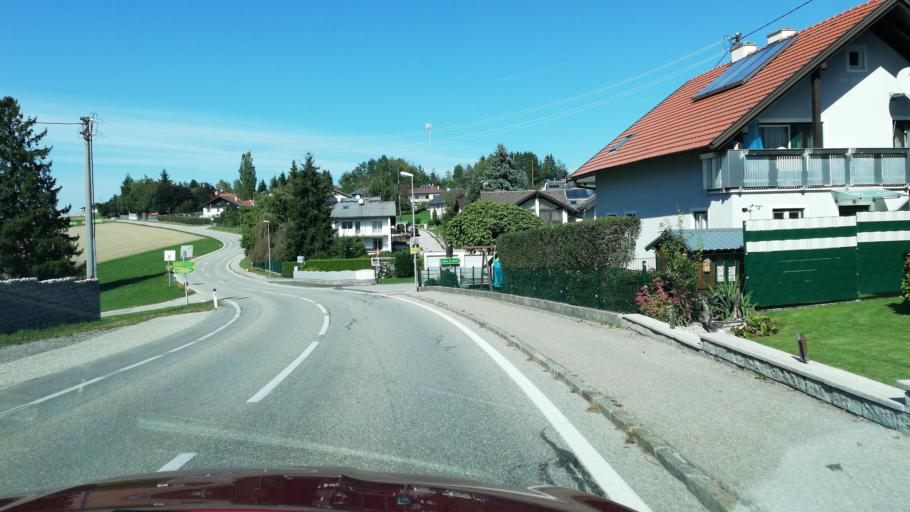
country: AT
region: Upper Austria
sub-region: Politischer Bezirk Vocklabruck
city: Zell am Pettenfirst
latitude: 48.1476
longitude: 13.5694
